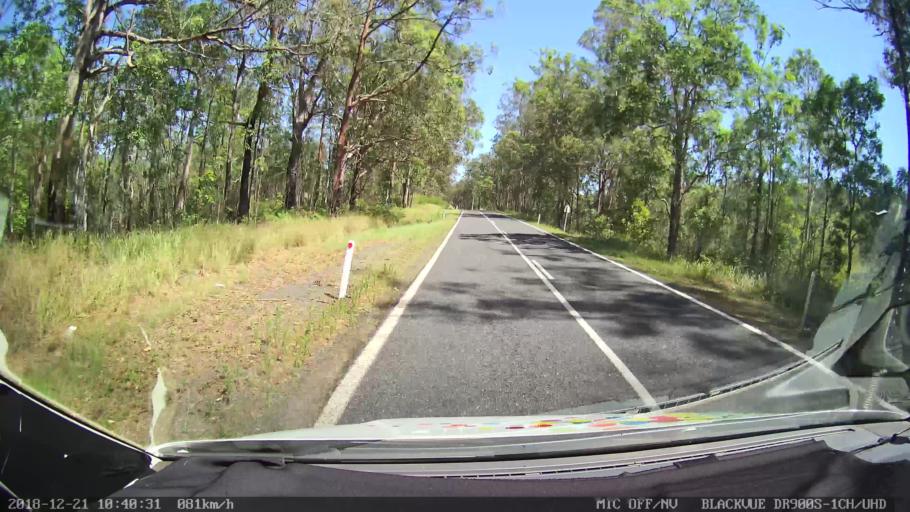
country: AU
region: New South Wales
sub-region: Clarence Valley
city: Gordon
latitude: -29.5989
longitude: 152.5851
